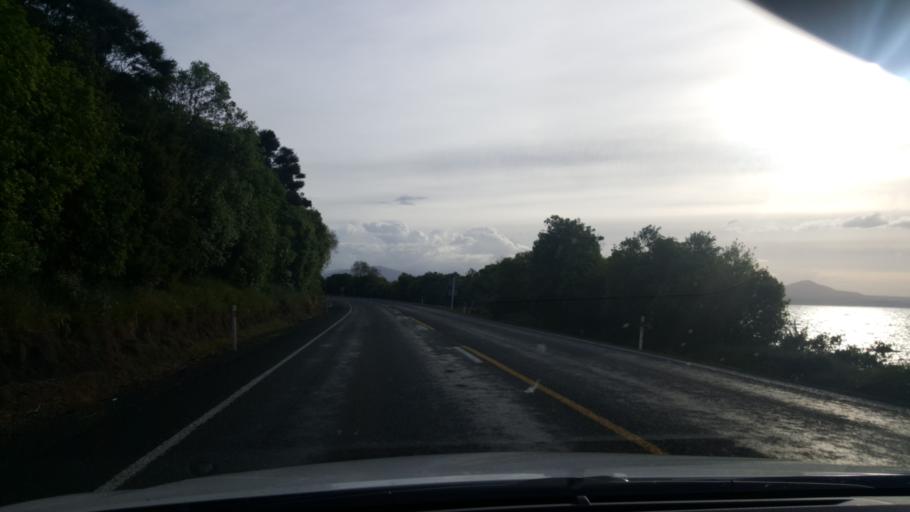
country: NZ
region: Waikato
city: Turangi
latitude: -38.8874
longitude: 175.9532
